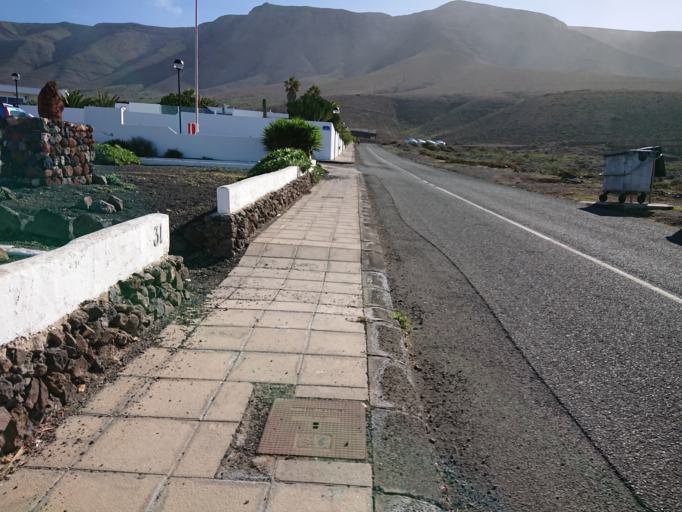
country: ES
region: Canary Islands
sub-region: Provincia de Las Palmas
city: Teguise
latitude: 29.1119
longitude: -13.5466
